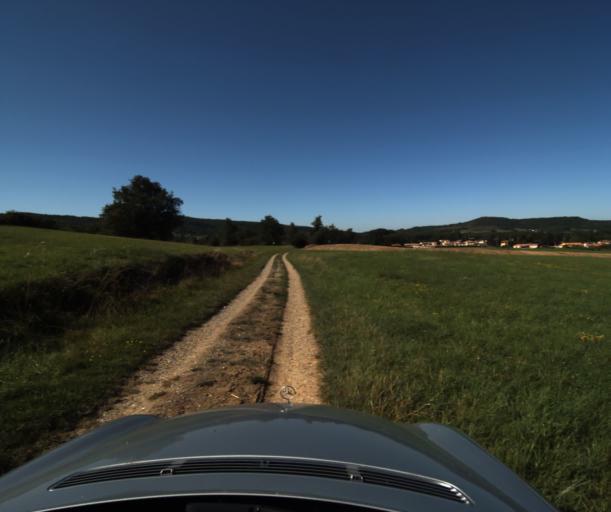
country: FR
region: Midi-Pyrenees
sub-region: Departement de l'Ariege
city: Lavelanet
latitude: 42.9821
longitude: 1.9113
